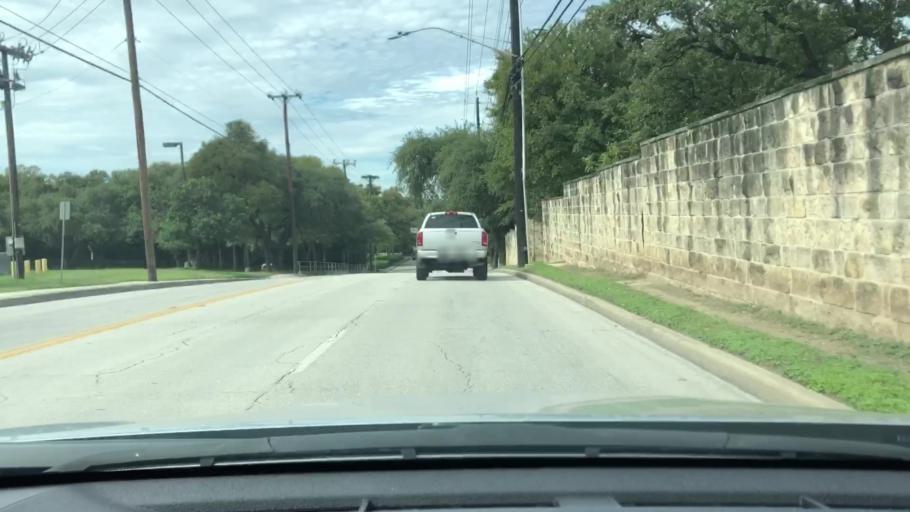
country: US
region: Texas
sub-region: Bexar County
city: Olmos Park
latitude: 29.4666
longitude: -98.4833
